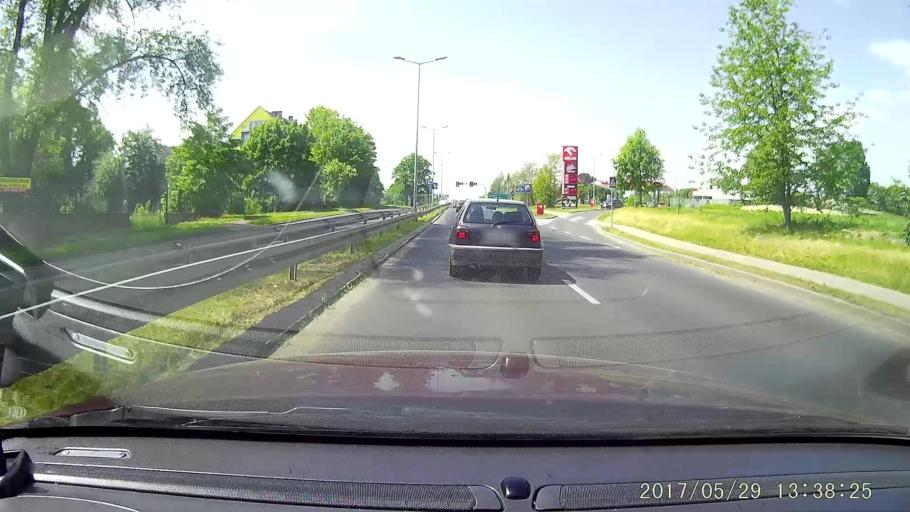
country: PL
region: Lower Silesian Voivodeship
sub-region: Powiat lubanski
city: Luban
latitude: 51.1225
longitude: 15.2939
